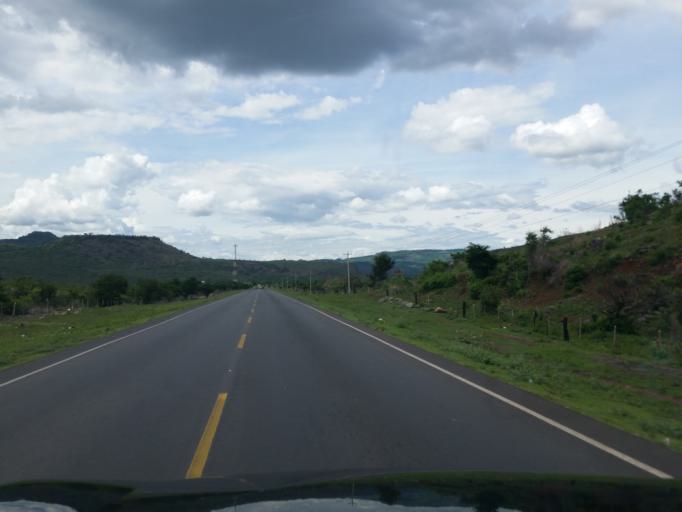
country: NI
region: Managua
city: Tipitapa
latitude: 12.4264
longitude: -86.0418
